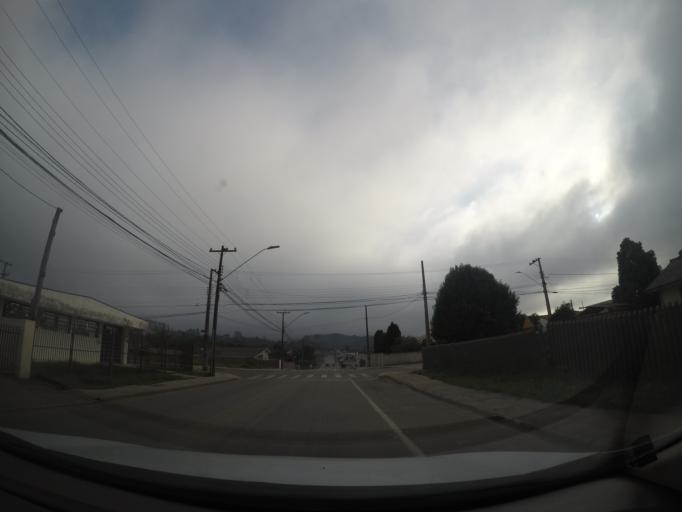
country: BR
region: Parana
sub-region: Colombo
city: Colombo
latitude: -25.2924
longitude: -49.2306
